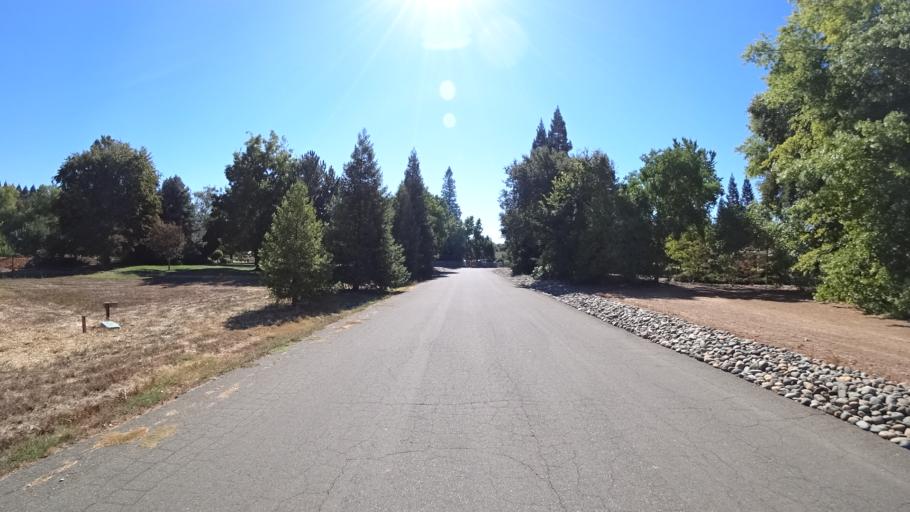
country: US
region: California
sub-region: Sacramento County
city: Wilton
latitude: 38.4178
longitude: -121.3036
